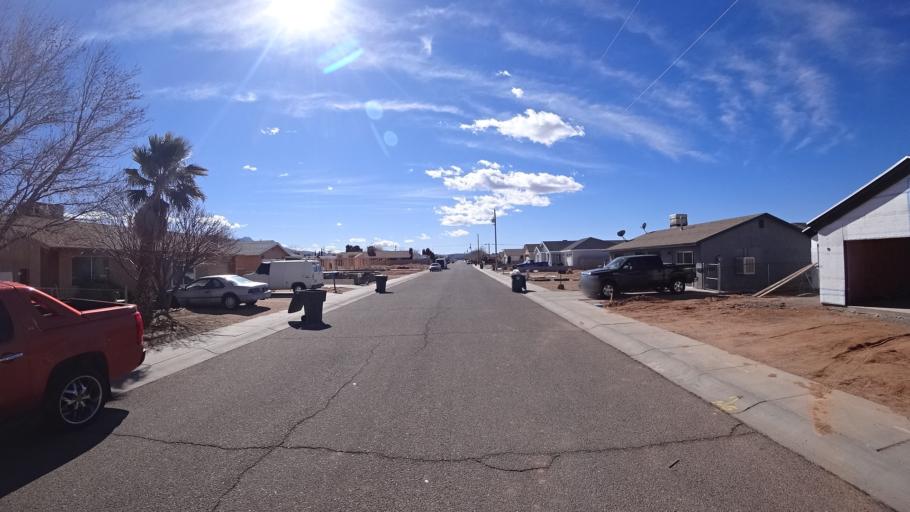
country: US
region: Arizona
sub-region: Mohave County
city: New Kingman-Butler
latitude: 35.2297
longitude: -114.0191
